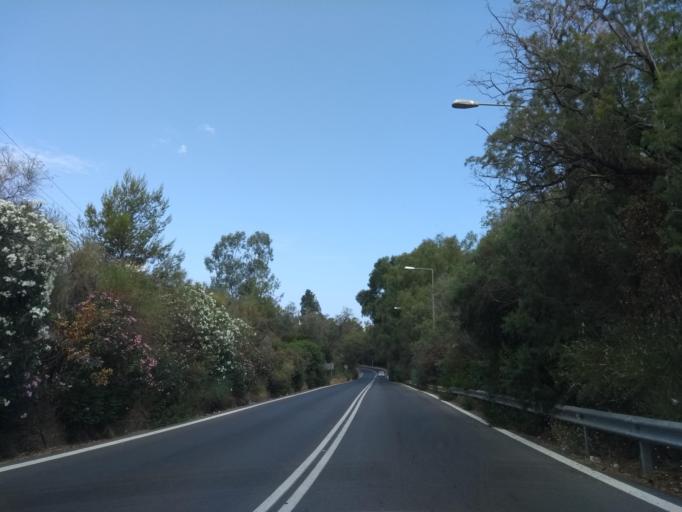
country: GR
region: Crete
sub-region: Nomos Chanias
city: Souda
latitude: 35.4827
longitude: 24.0944
